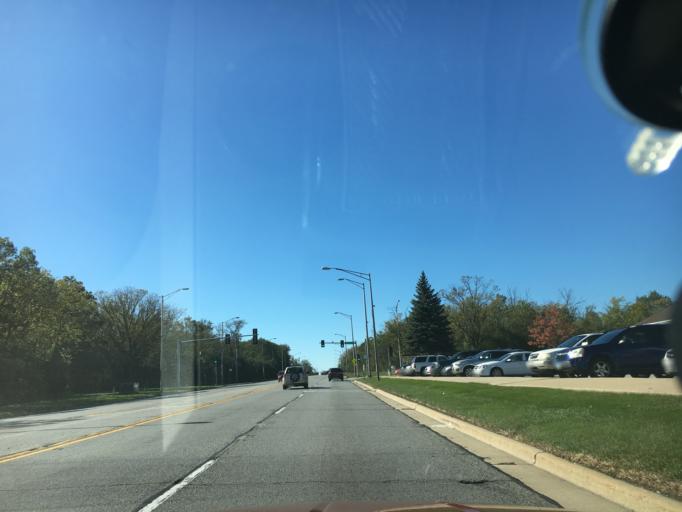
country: US
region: Illinois
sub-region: Cook County
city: Oak Forest
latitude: 41.6027
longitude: -87.7741
